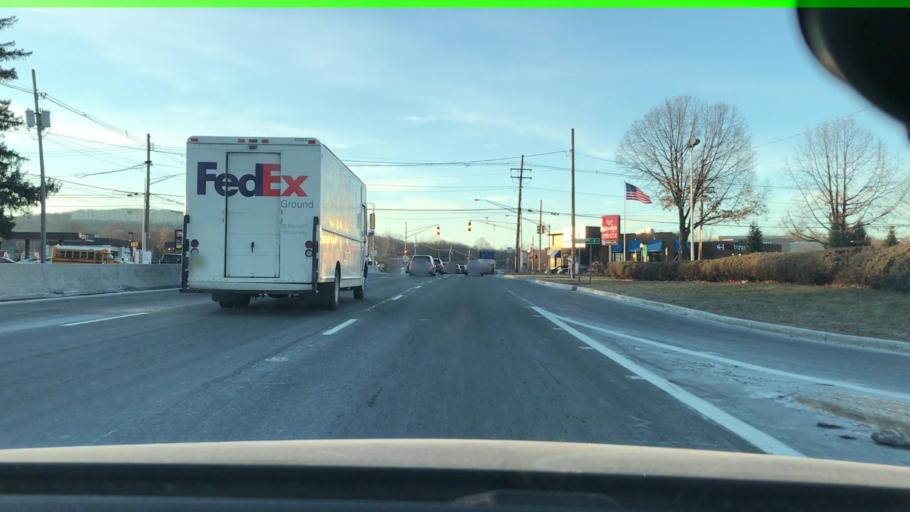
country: US
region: New Jersey
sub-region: Morris County
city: Morris Plains
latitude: 40.8433
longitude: -74.4628
